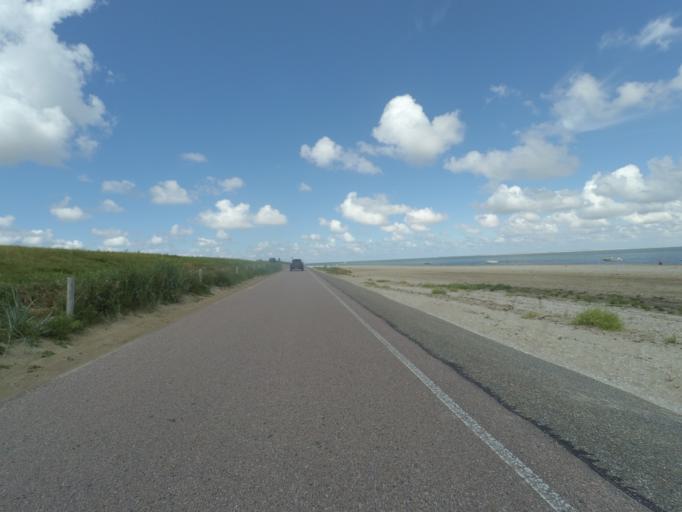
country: NL
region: North Holland
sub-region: Gemeente Texel
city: Den Burg
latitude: 53.1699
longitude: 4.8740
